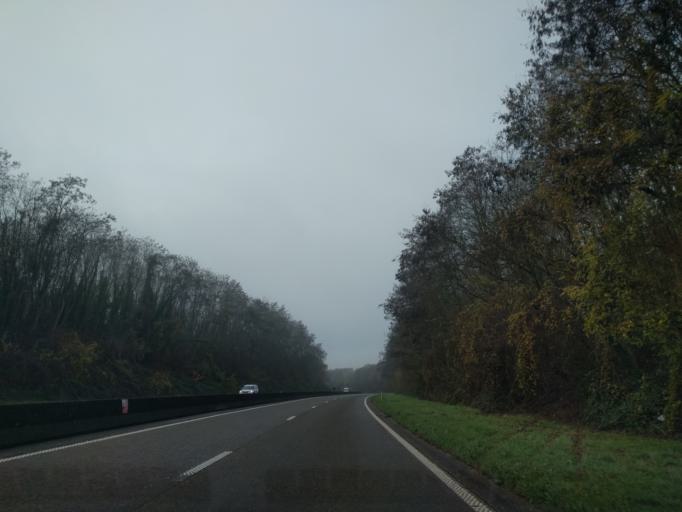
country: BE
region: Wallonia
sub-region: Province de Namur
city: Dinant
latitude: 50.2436
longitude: 4.9046
